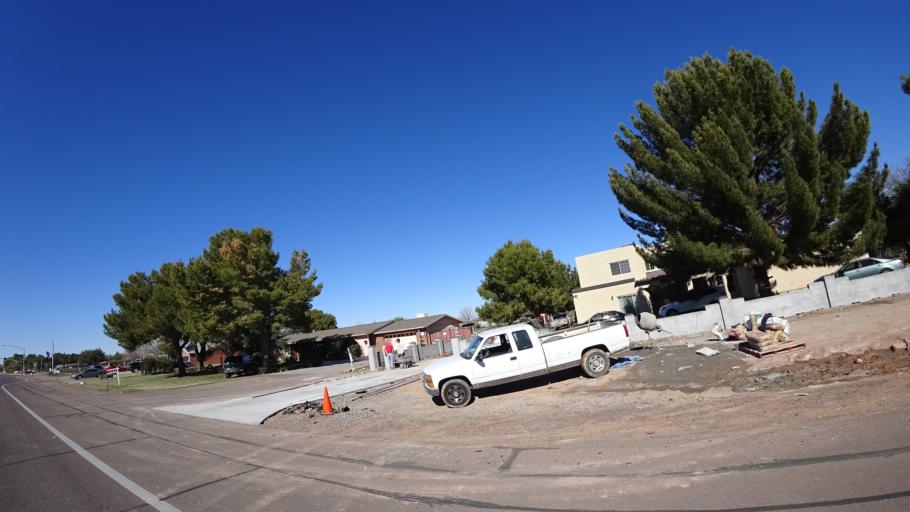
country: US
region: Arizona
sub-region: Maricopa County
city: Laveen
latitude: 33.3774
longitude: -112.2005
